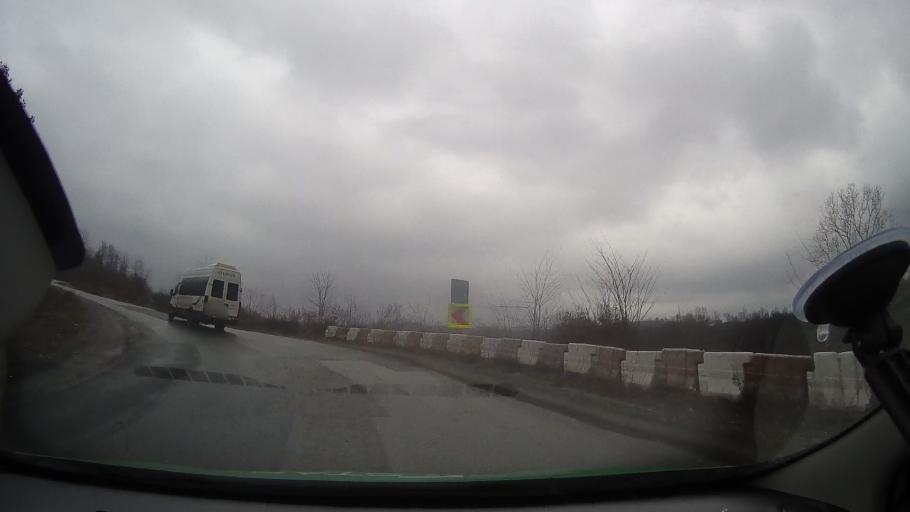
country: RO
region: Arad
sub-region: Comuna Halmagiu
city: Halmagiu
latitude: 46.2854
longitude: 22.5475
